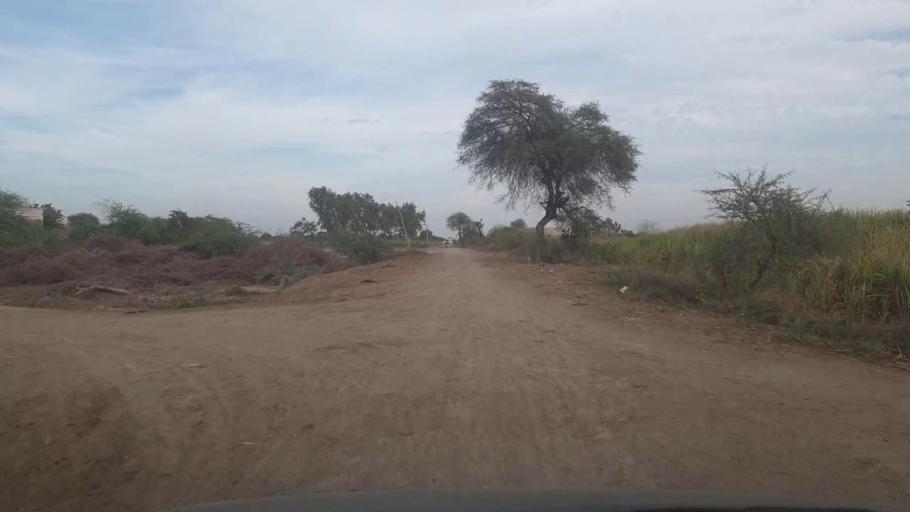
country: PK
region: Sindh
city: Samaro
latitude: 25.3235
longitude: 69.2603
